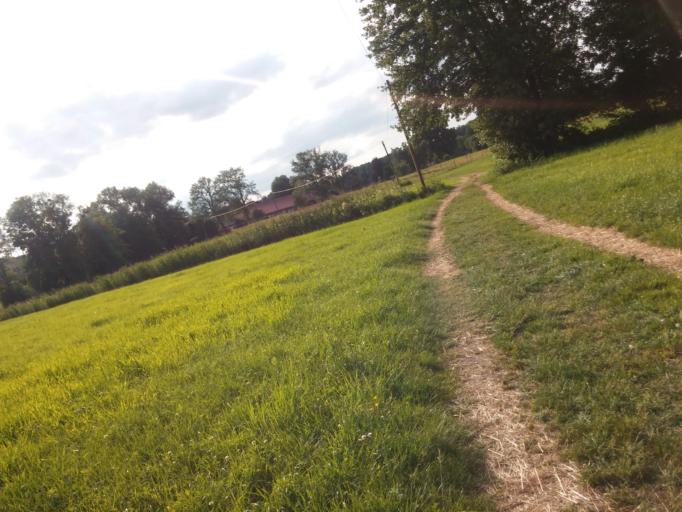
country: DE
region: Bavaria
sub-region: Upper Bavaria
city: Moosach
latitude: 48.0200
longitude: 11.8575
